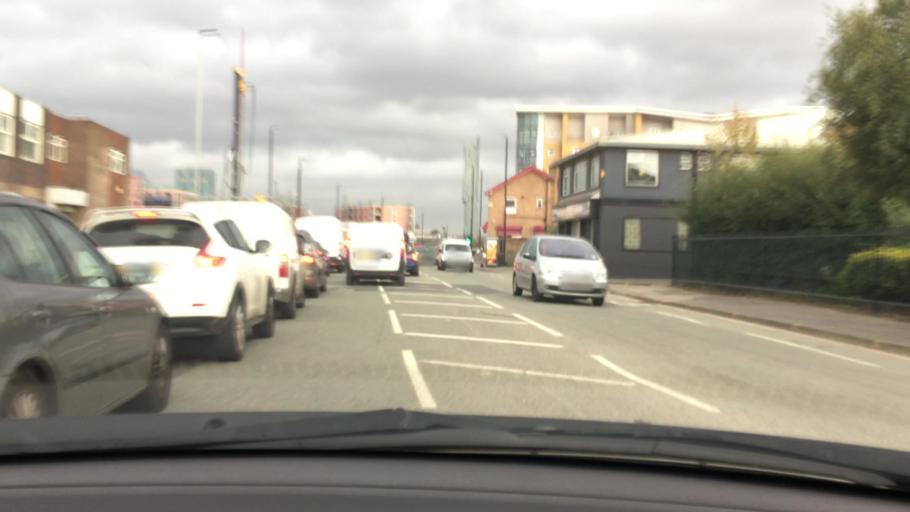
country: GB
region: England
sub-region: City and Borough of Salford
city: Salford
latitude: 53.4800
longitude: -2.2687
